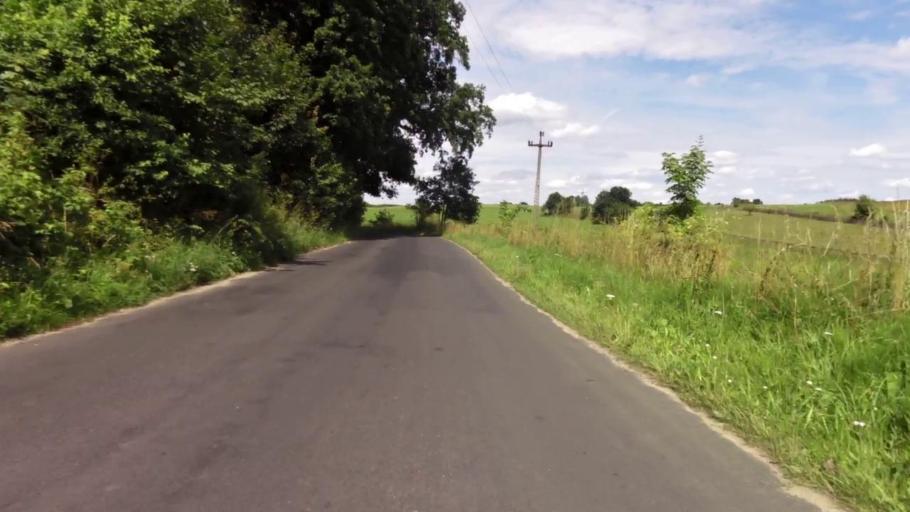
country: PL
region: West Pomeranian Voivodeship
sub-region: Powiat stargardzki
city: Dobrzany
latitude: 53.4258
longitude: 15.4677
